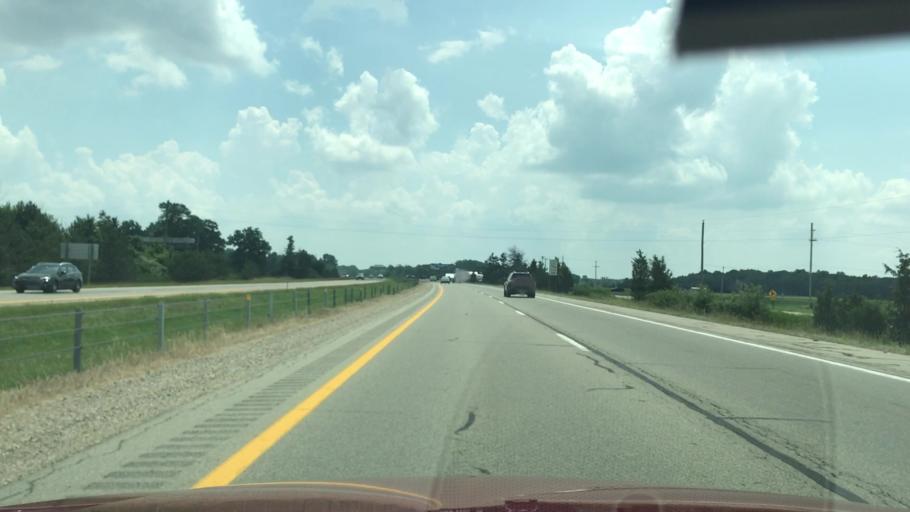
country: US
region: Michigan
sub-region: Allegan County
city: Wayland
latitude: 42.6221
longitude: -85.6625
